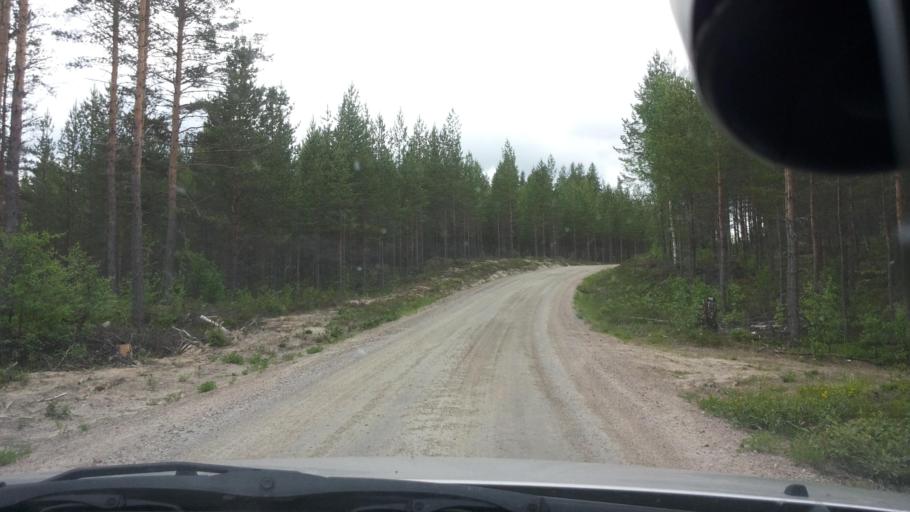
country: SE
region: Gaevleborg
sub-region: Ovanakers Kommun
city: Edsbyn
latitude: 61.5207
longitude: 15.3560
